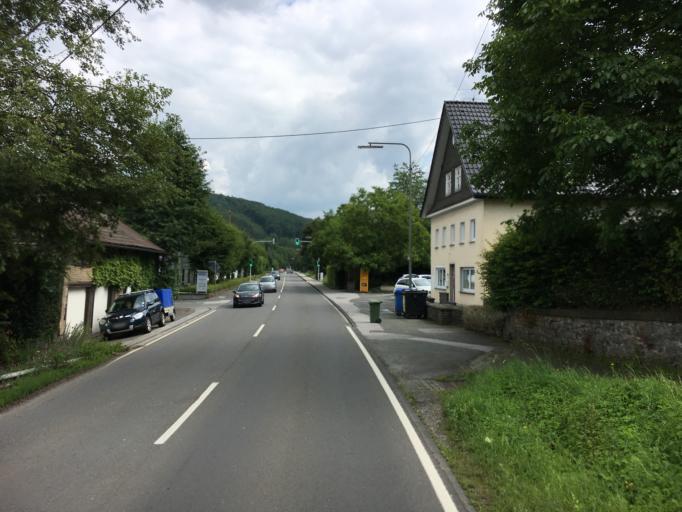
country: DE
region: North Rhine-Westphalia
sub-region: Regierungsbezirk Arnsberg
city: Lennestadt
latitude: 51.1301
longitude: 8.0299
